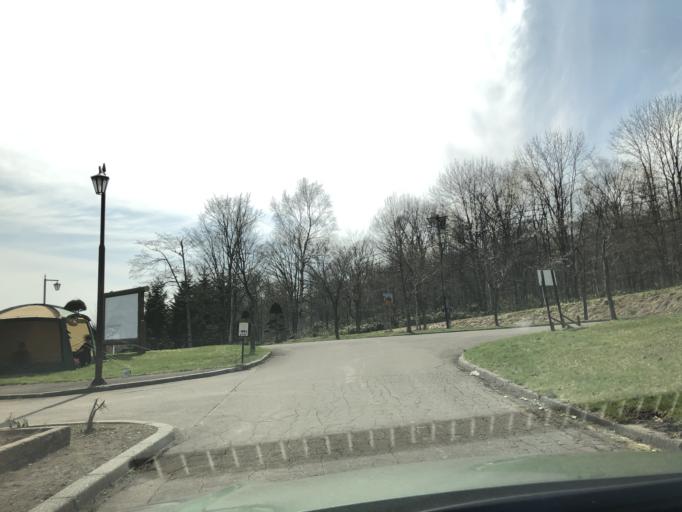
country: JP
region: Hokkaido
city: Akabira
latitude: 43.5941
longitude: 142.0456
